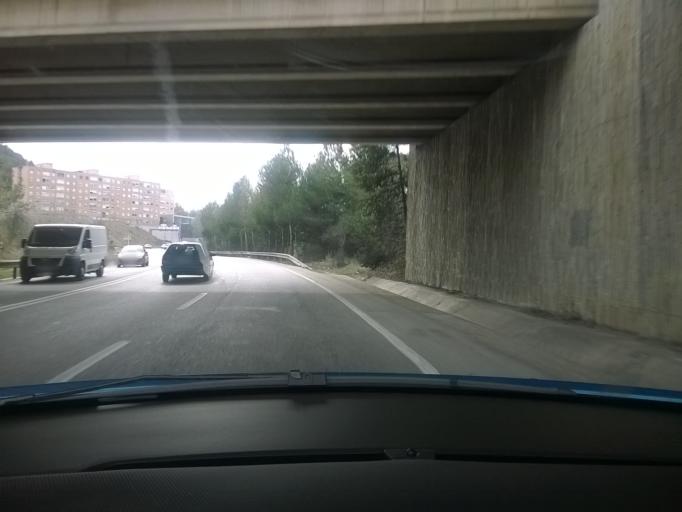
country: ES
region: Catalonia
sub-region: Provincia de Barcelona
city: Rubi
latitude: 41.5105
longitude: 2.0482
